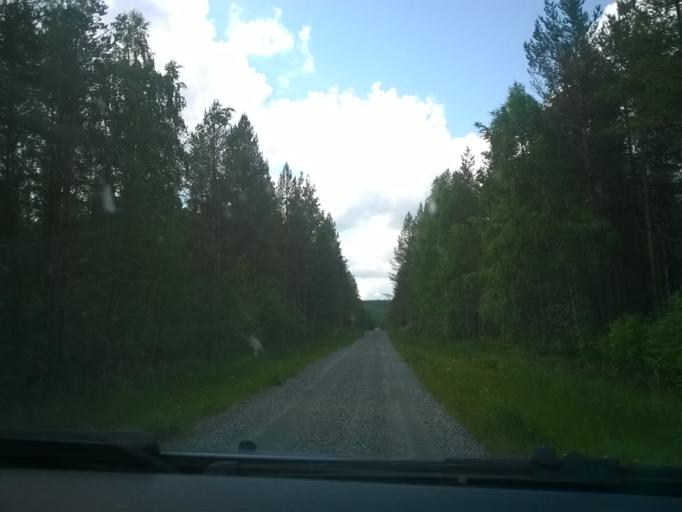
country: FI
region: Kainuu
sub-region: Kehys-Kainuu
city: Kuhmo
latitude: 64.4543
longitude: 29.6991
